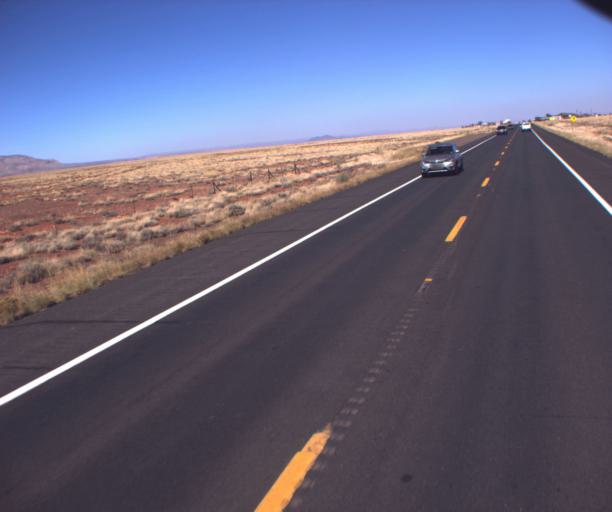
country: US
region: Arizona
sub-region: Coconino County
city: Tuba City
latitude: 35.7351
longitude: -111.4784
